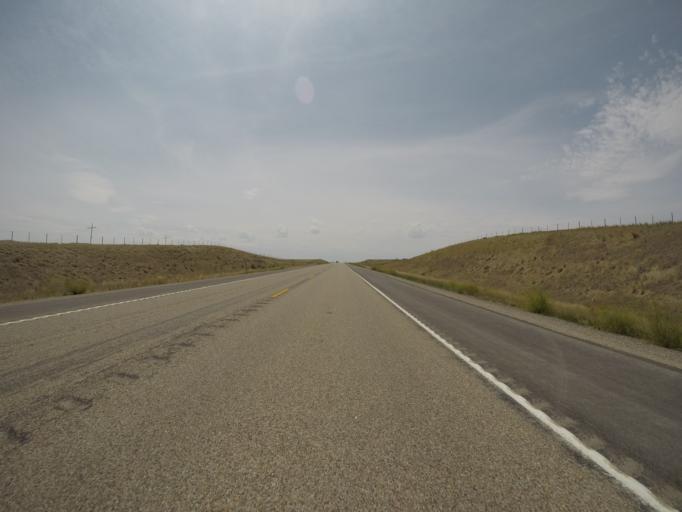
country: US
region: Wyoming
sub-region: Lincoln County
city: Kemmerer
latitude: 41.6983
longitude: -110.5664
